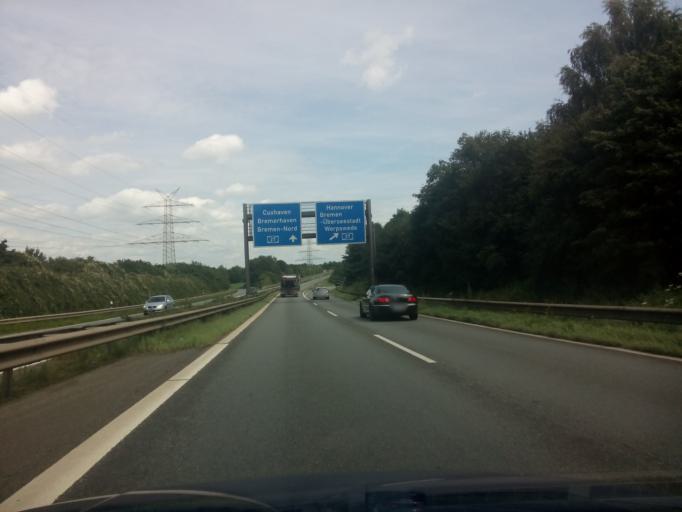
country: DE
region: Lower Saxony
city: Ritterhude
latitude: 53.1448
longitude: 8.7275
